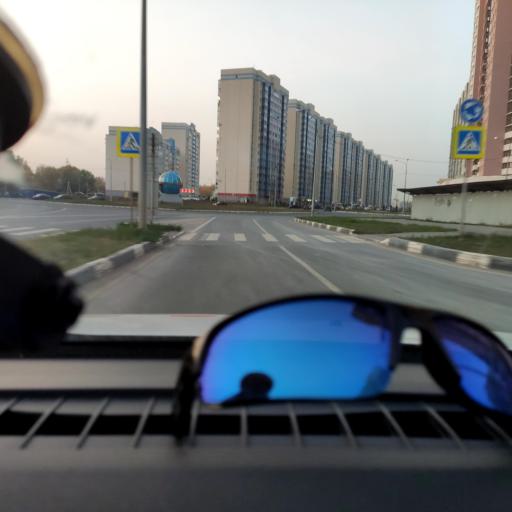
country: RU
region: Samara
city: Rozhdestveno
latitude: 53.1478
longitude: 50.0749
